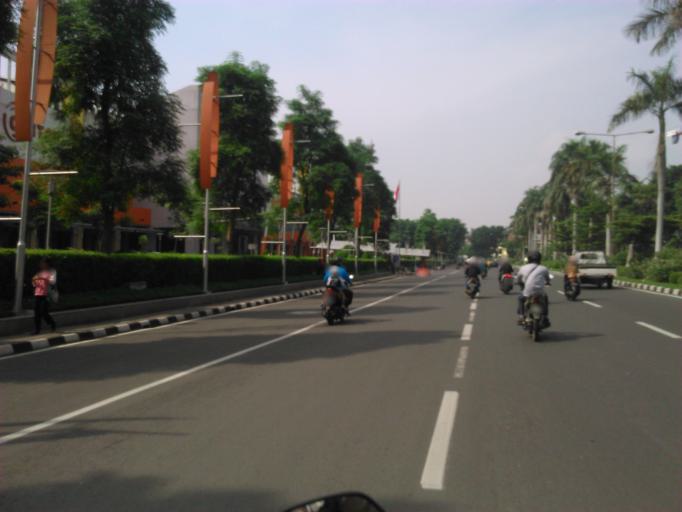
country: ID
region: East Java
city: Mulyorejo
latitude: -7.2751
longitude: 112.7817
